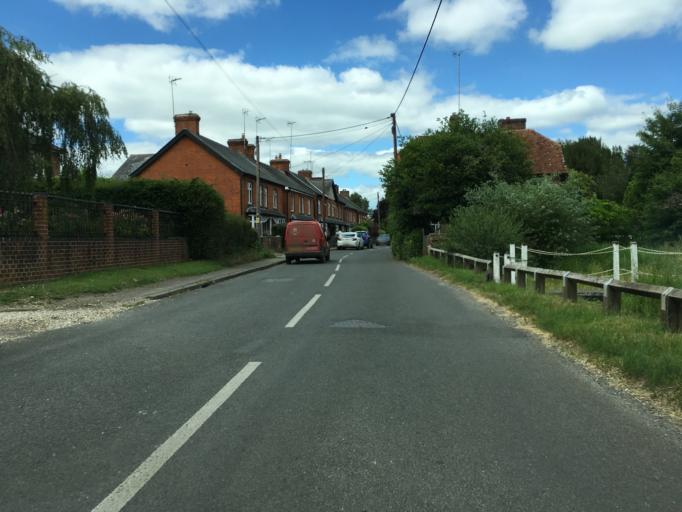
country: GB
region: England
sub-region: Hampshire
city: Highclere
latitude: 51.2538
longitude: -1.4018
